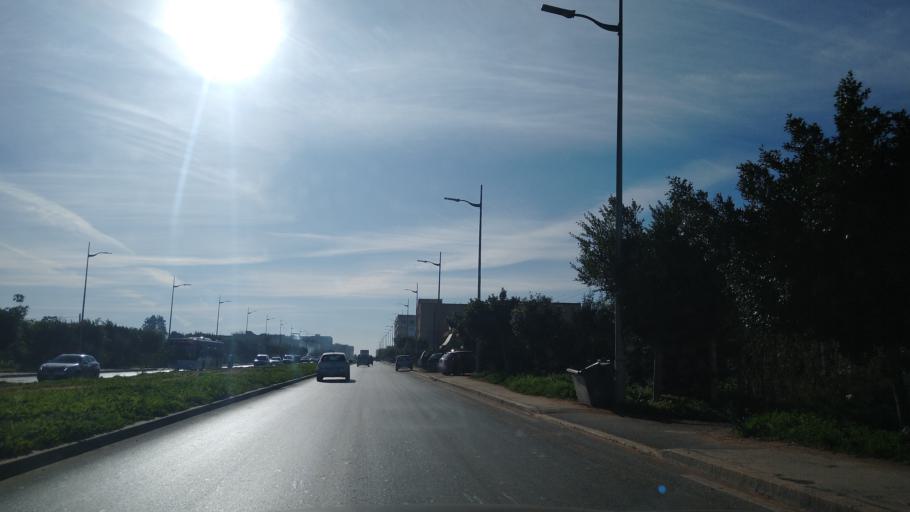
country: MA
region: Rabat-Sale-Zemmour-Zaer
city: Sale
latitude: 34.0108
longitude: -6.7385
